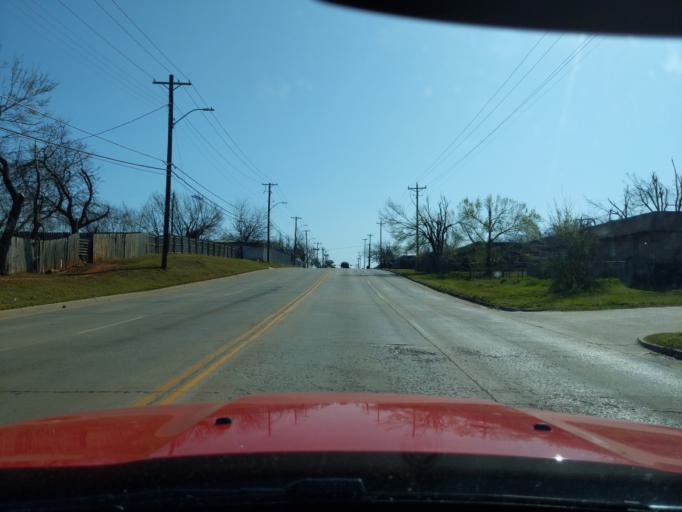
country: US
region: Oklahoma
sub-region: Cleveland County
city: Moore
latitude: 35.3488
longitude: -97.4885
